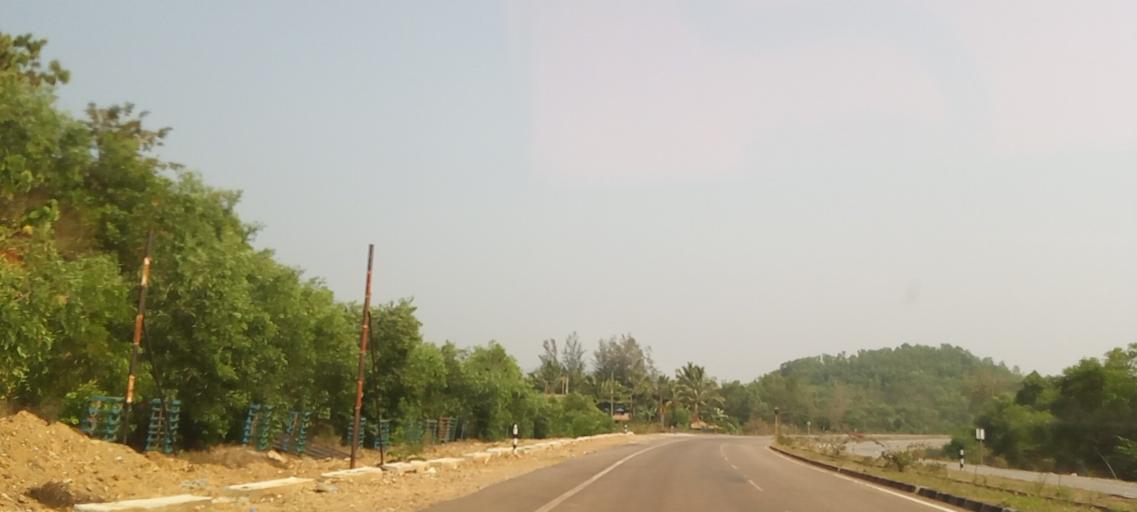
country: IN
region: Karnataka
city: Canacona
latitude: 14.9079
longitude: 74.0964
